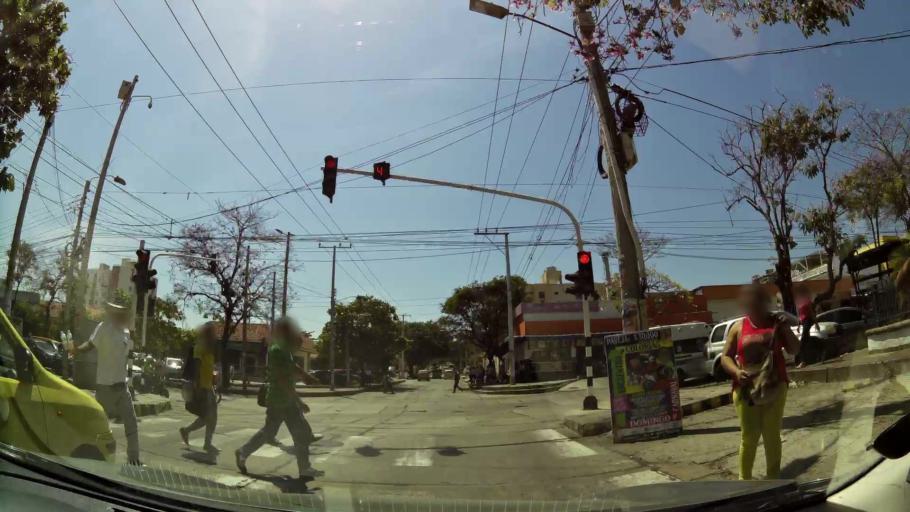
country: CO
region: Atlantico
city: Barranquilla
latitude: 10.9905
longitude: -74.8048
